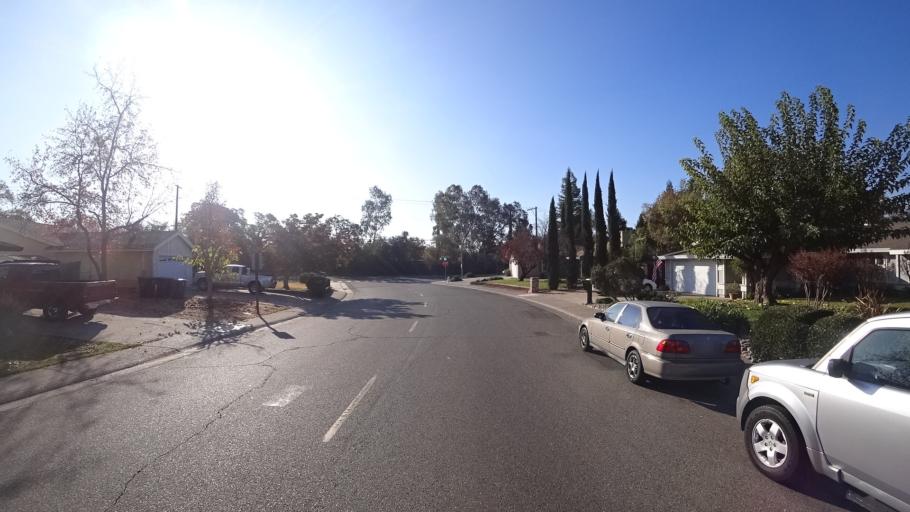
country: US
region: California
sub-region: Sacramento County
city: Citrus Heights
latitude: 38.7090
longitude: -121.2620
